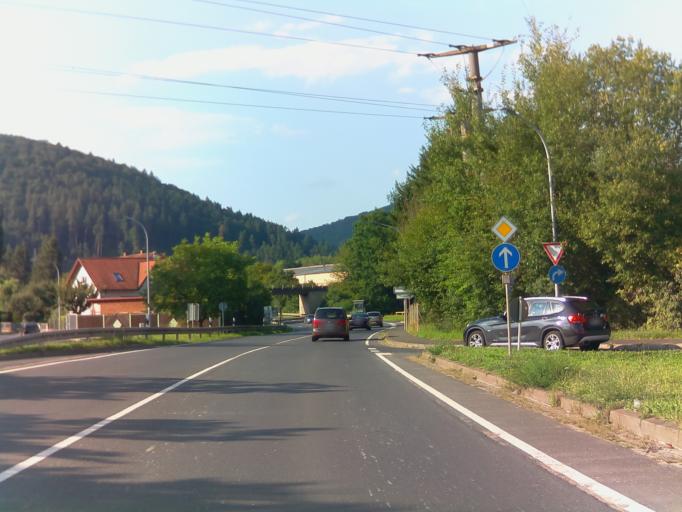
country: DE
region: Bavaria
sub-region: Regierungsbezirk Unterfranken
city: Gemunden
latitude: 50.0597
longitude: 9.6845
